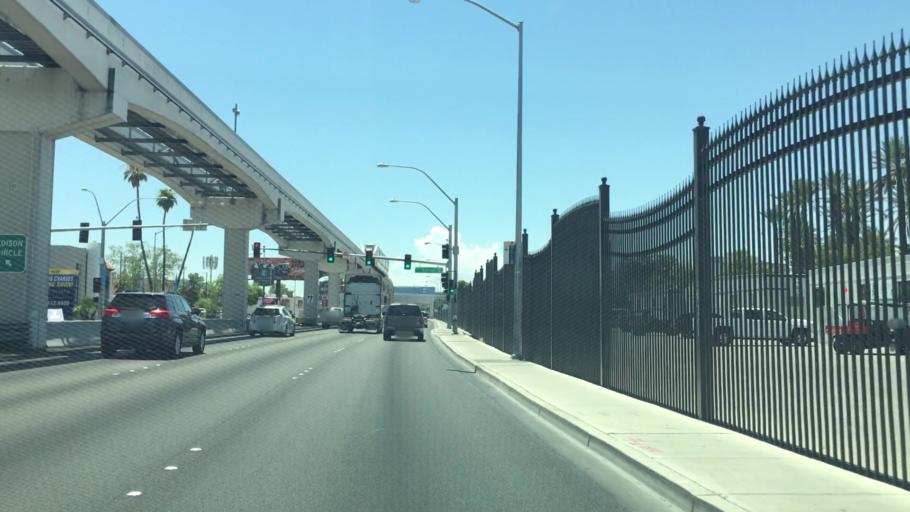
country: US
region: Nevada
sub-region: Clark County
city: Paradise
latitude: 36.1255
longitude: -115.1551
